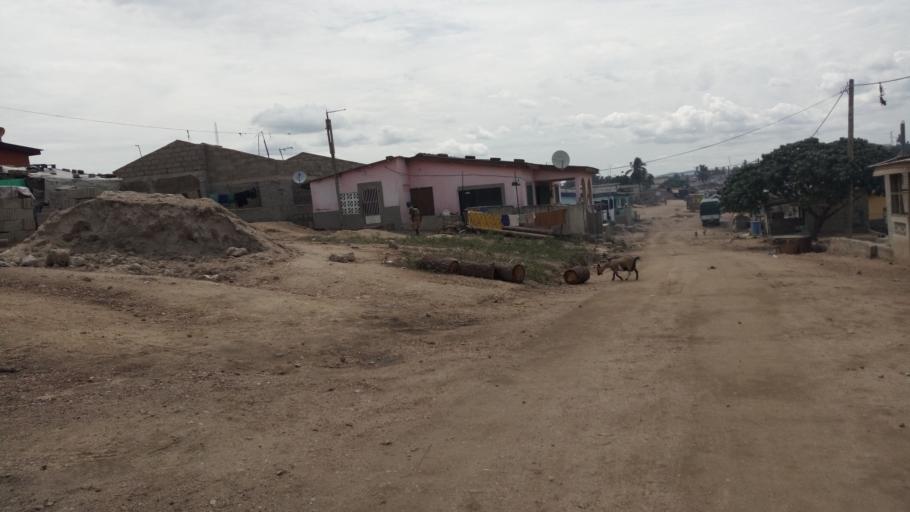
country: GH
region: Central
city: Winneba
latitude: 5.3474
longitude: -0.6148
